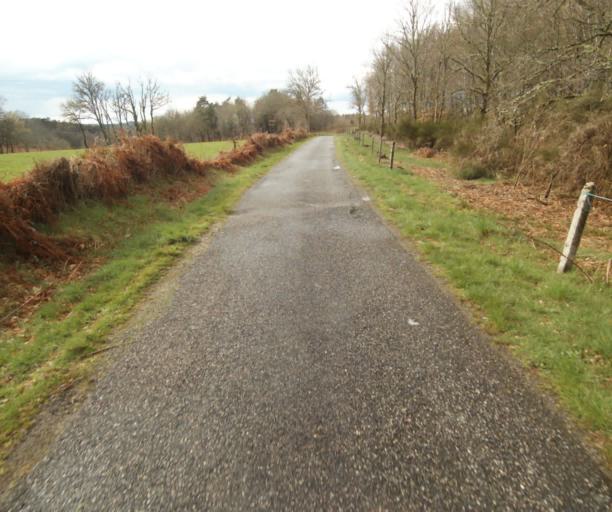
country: FR
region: Limousin
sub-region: Departement de la Correze
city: Saint-Privat
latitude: 45.2430
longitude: 2.0041
